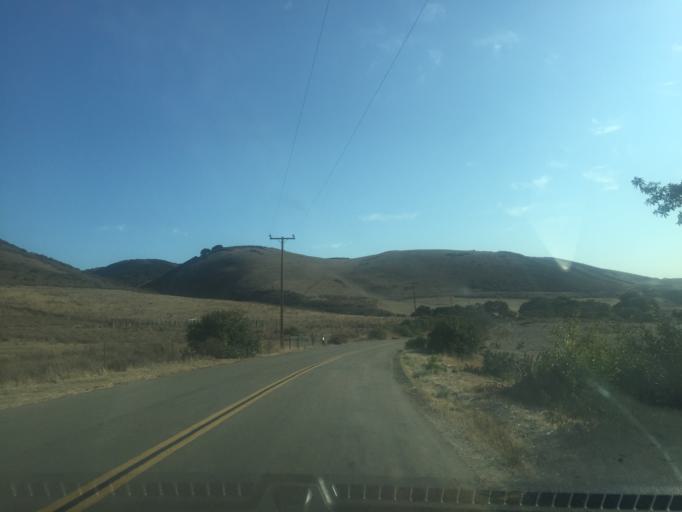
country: US
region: California
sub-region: Santa Barbara County
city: Lompoc
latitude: 34.5148
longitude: -120.4777
